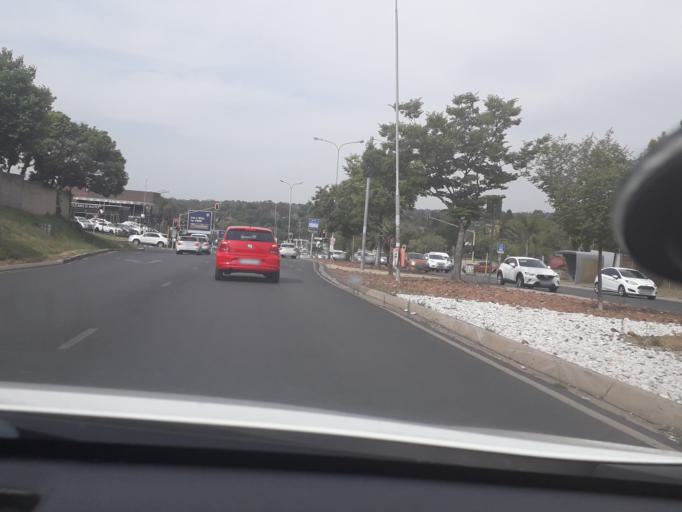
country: ZA
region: Gauteng
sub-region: City of Johannesburg Metropolitan Municipality
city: Johannesburg
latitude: -26.0914
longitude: 28.0230
